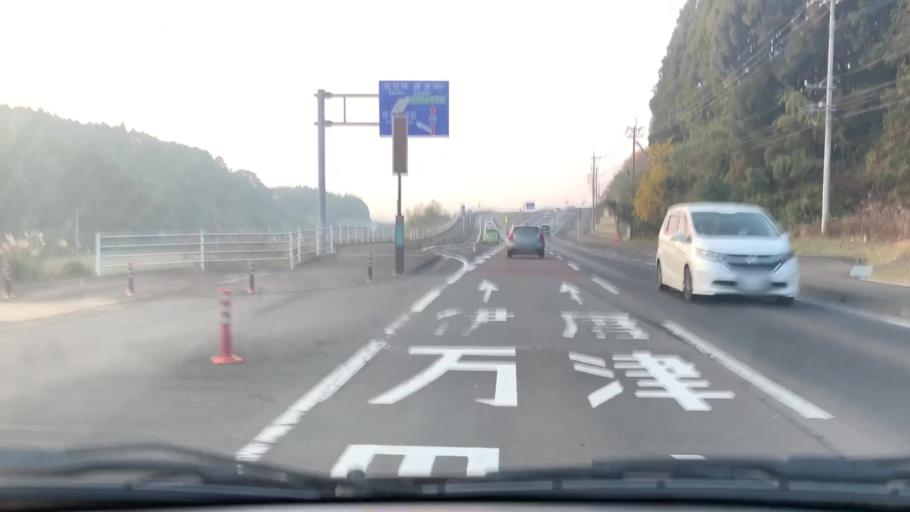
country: JP
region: Saga Prefecture
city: Imaricho-ko
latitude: 33.2621
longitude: 129.9117
